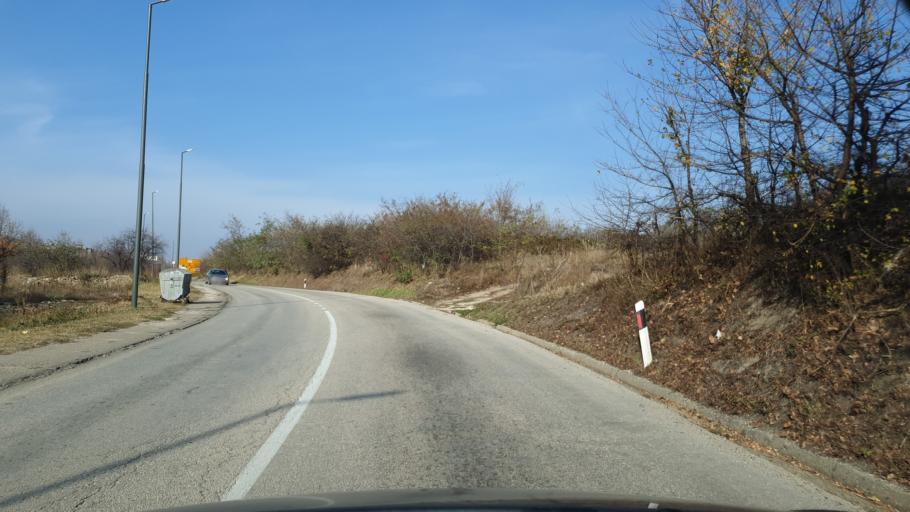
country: RS
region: Central Serbia
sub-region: Borski Okrug
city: Bor
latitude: 44.0533
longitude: 22.1045
